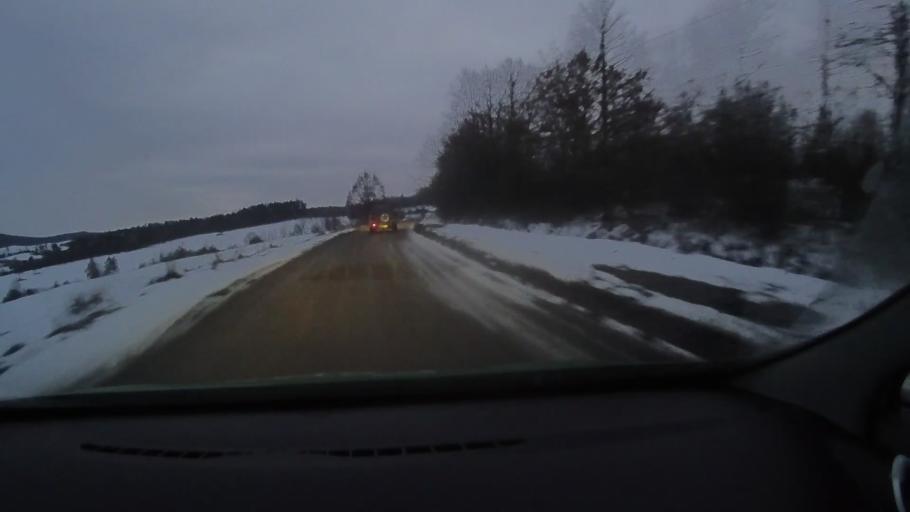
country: RO
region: Harghita
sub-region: Comuna Darjiu
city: Darjiu
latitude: 46.1886
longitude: 25.2474
